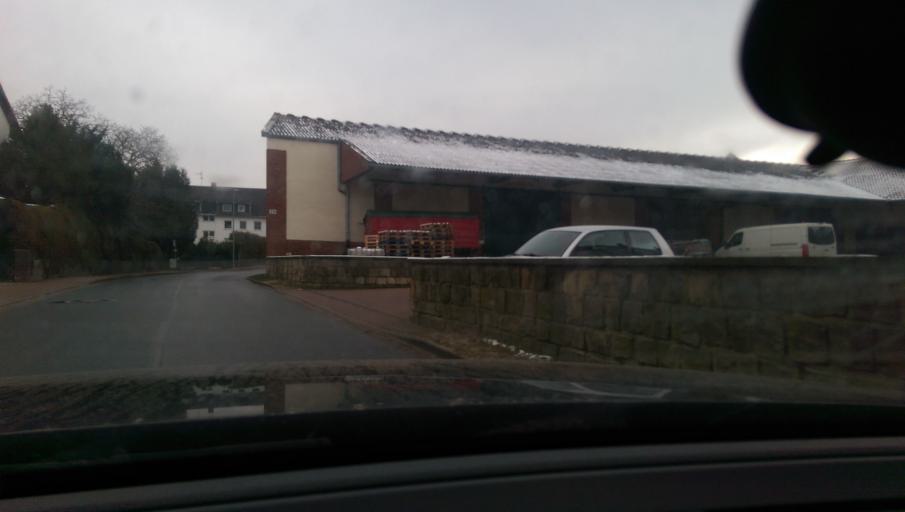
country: DE
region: Lower Saxony
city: Wennigsen
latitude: 52.2880
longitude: 9.5697
